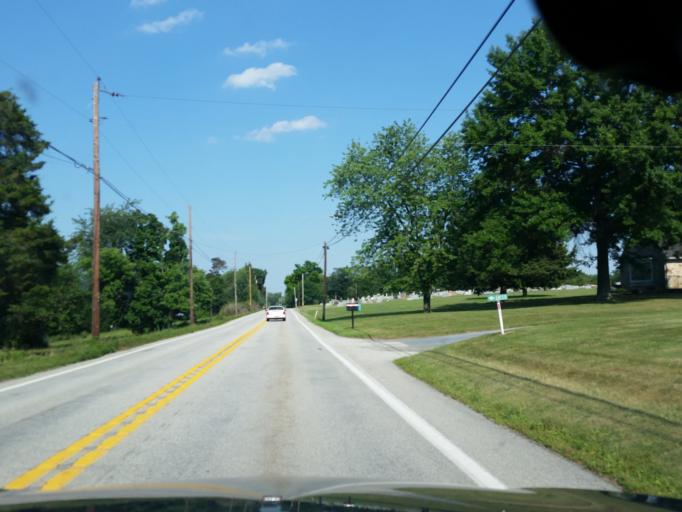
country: US
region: Pennsylvania
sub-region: Cumberland County
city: Mechanicsburg
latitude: 40.2860
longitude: -77.0183
